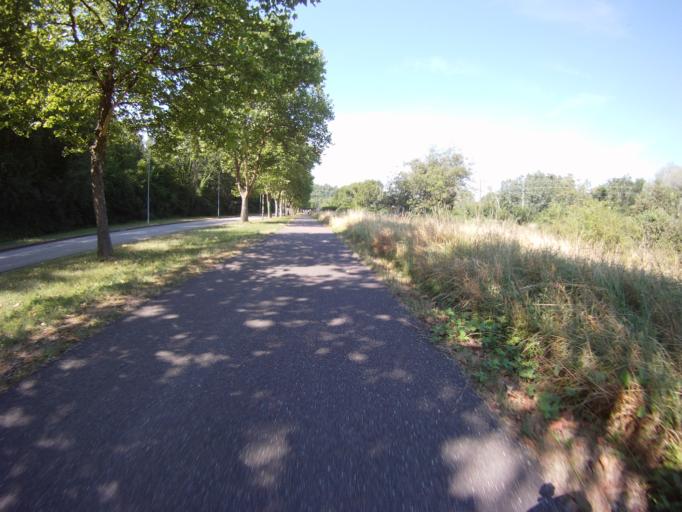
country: FR
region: Lorraine
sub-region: Departement de Meurthe-et-Moselle
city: Liverdun
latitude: 48.7494
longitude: 6.0802
